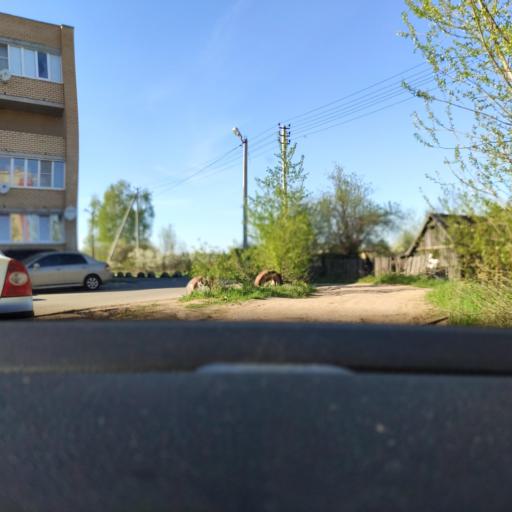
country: RU
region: Moskovskaya
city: Dmitrov
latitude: 56.3577
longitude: 37.5701
